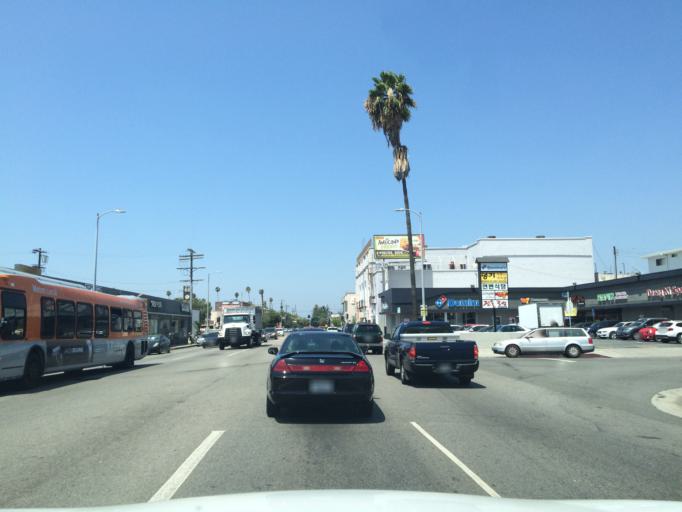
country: US
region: California
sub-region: Los Angeles County
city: Hollywood
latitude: 34.0690
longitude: -118.3064
